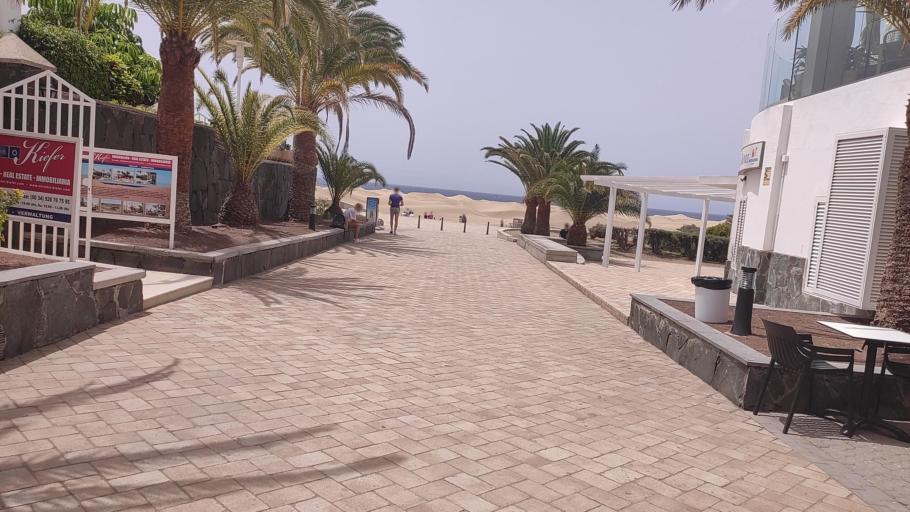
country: ES
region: Canary Islands
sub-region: Provincia de Las Palmas
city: Playa del Ingles
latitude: 27.7459
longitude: -15.5766
